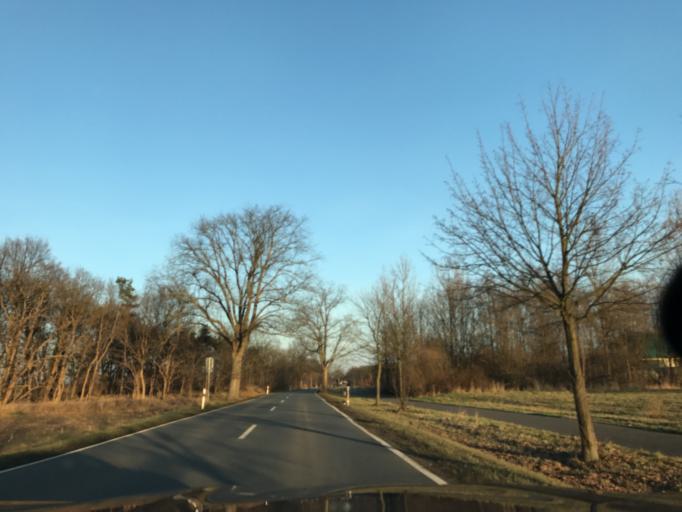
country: DE
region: Saxony-Anhalt
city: Genthin
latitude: 52.4201
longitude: 12.1641
